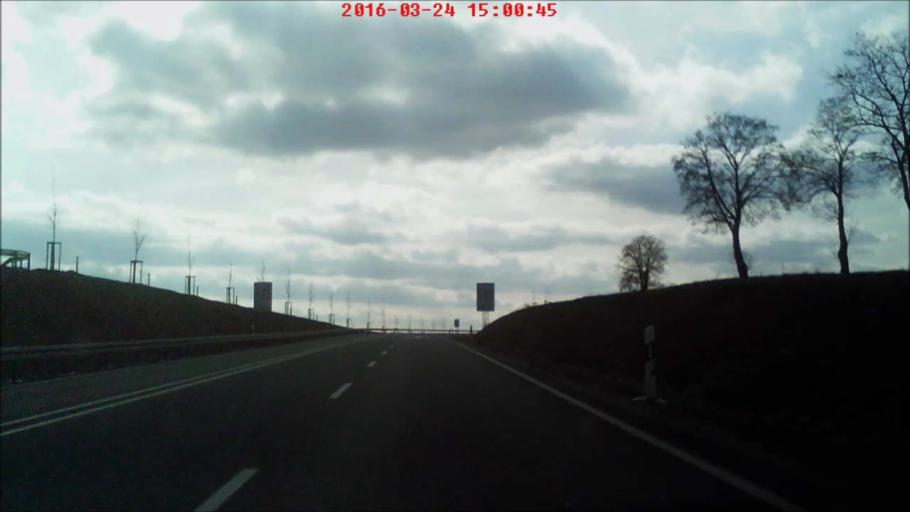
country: DE
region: Thuringia
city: Bad Blankenburg
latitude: 50.7316
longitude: 11.2408
